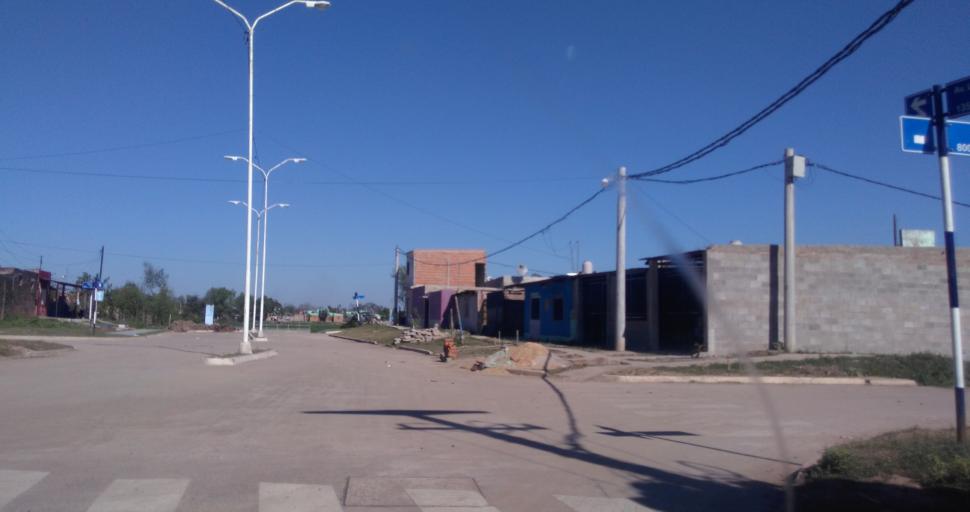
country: AR
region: Chaco
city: Resistencia
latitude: -27.4554
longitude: -58.9673
